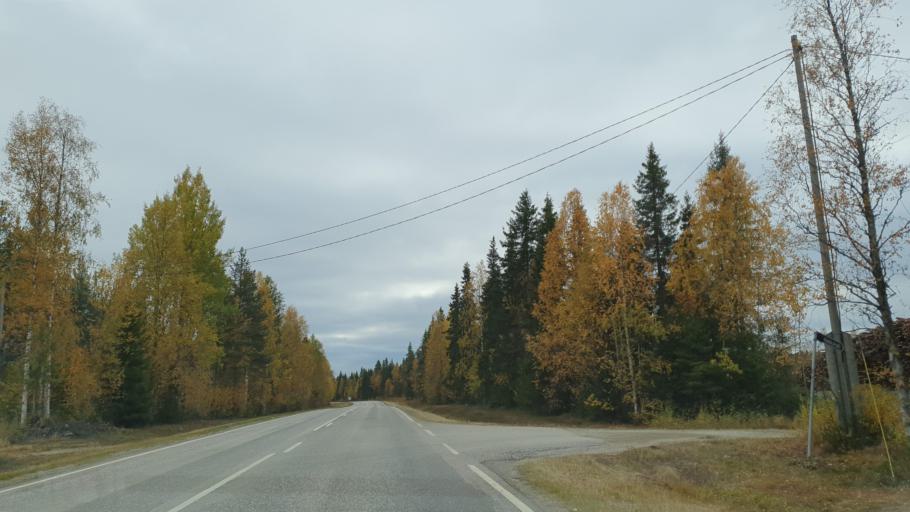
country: FI
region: Lapland
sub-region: Rovaniemi
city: Ranua
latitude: 65.9079
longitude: 26.5178
